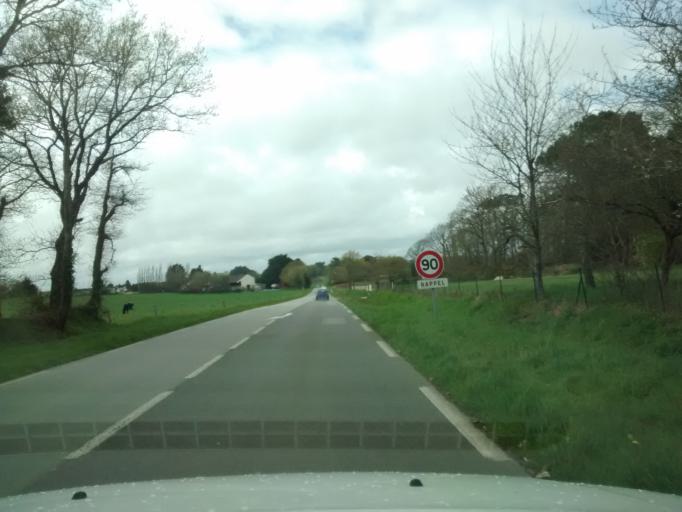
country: FR
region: Brittany
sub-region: Departement du Morbihan
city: Gestel
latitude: 47.7861
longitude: -3.4513
